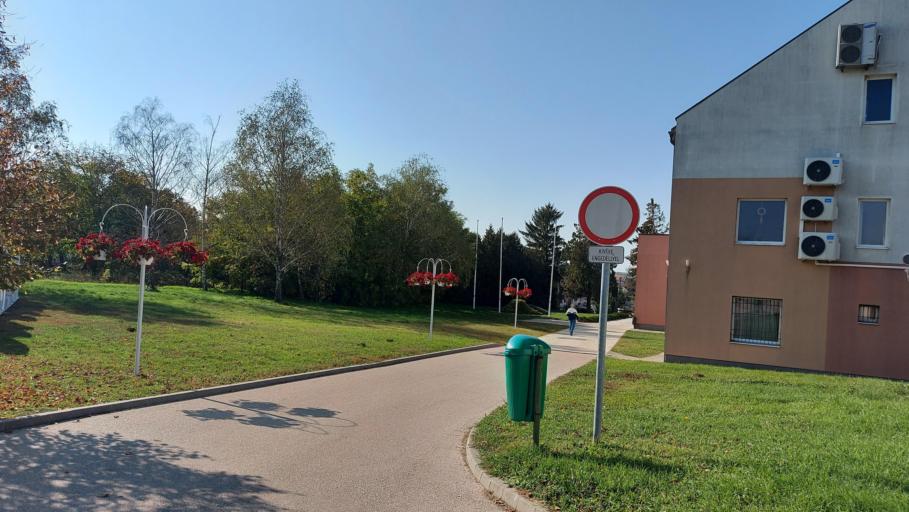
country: HU
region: Fejer
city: Polgardi
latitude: 47.0614
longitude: 18.2978
